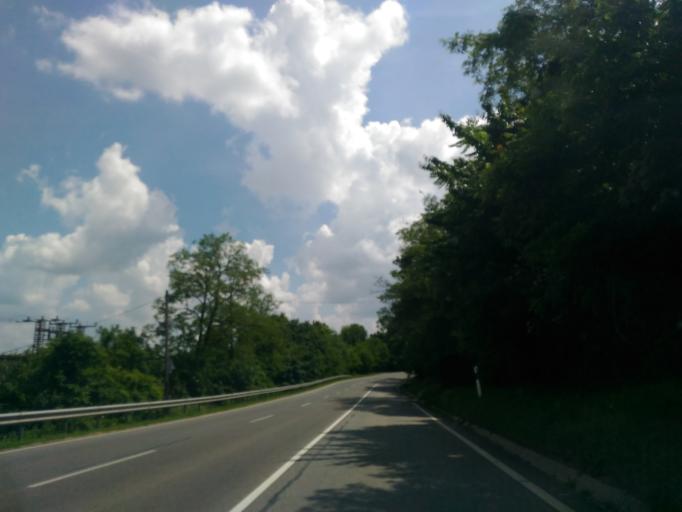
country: HU
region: Baranya
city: Pecs
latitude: 46.1234
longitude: 18.2606
